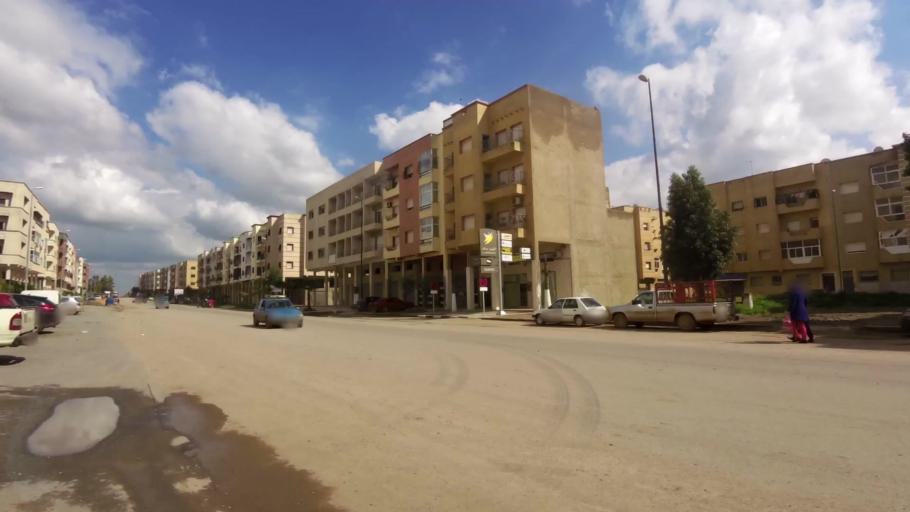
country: MA
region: Chaouia-Ouardigha
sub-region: Settat Province
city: Berrechid
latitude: 33.2626
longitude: -7.5671
